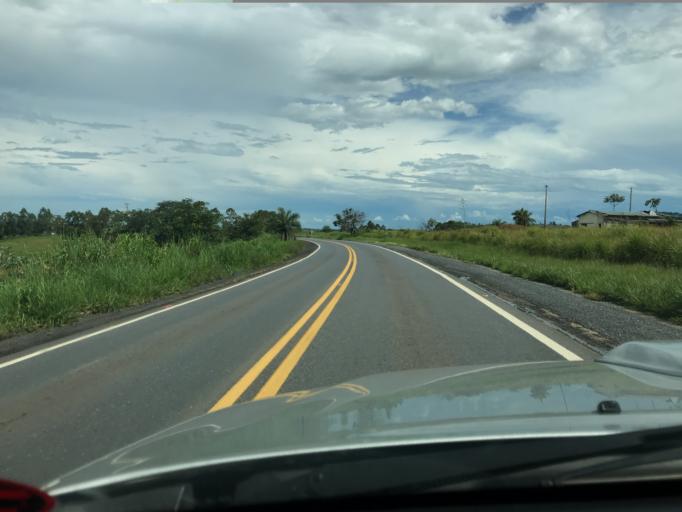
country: BR
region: Minas Gerais
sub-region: Campos Altos
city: Campos Altos
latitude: -19.8041
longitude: -46.0344
